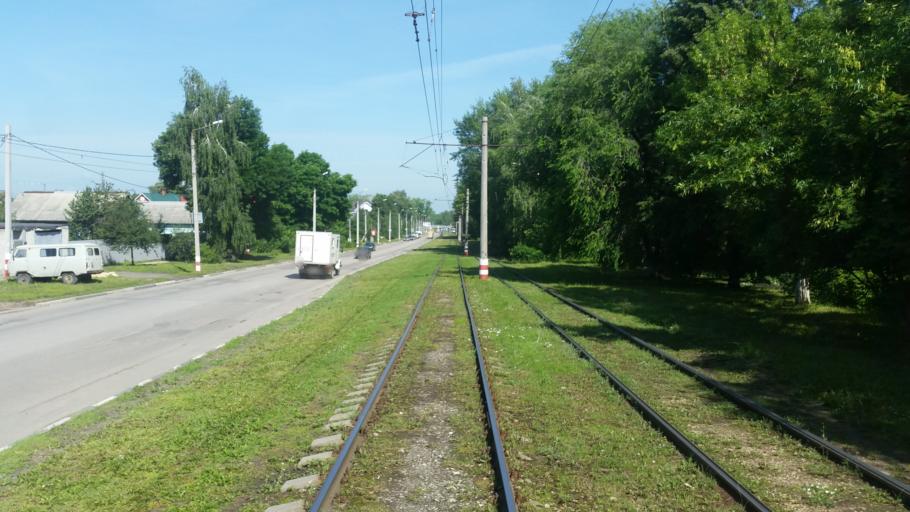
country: RU
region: Ulyanovsk
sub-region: Ulyanovskiy Rayon
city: Ulyanovsk
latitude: 54.3533
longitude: 48.3795
